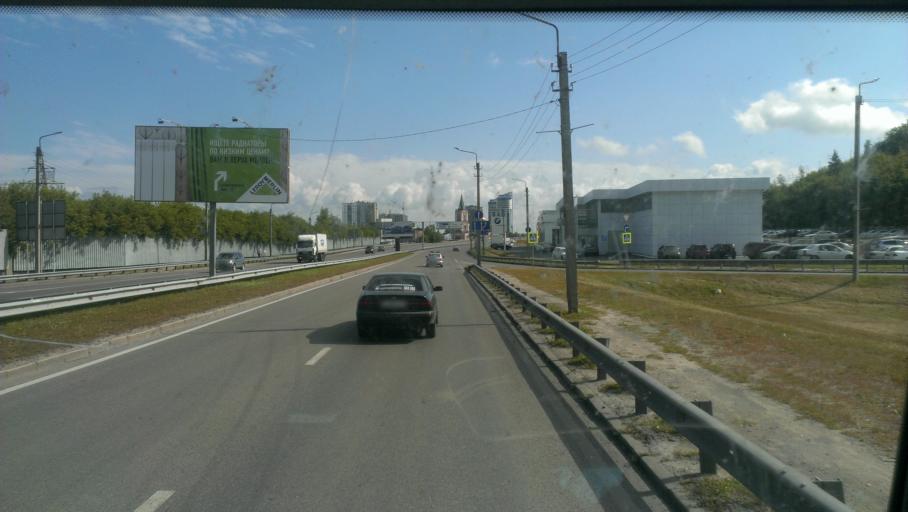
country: RU
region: Altai Krai
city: Zaton
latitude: 53.3245
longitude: 83.7900
